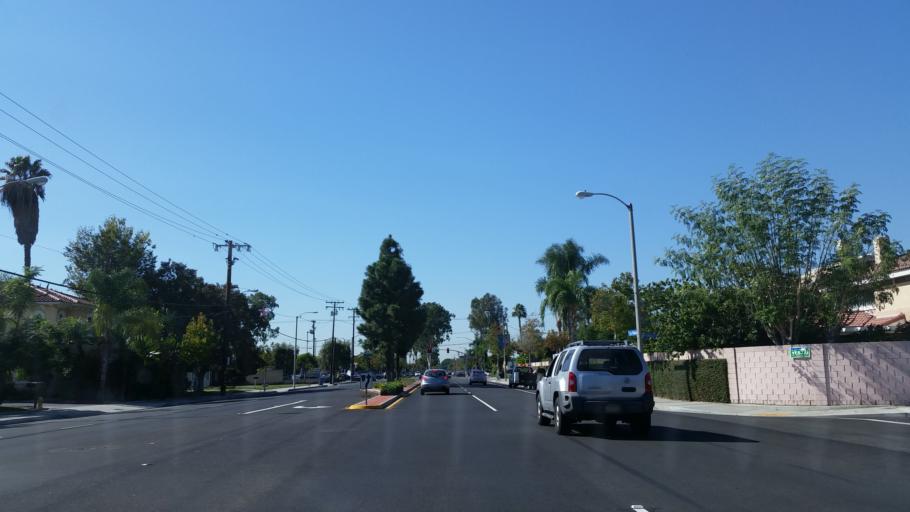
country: US
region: California
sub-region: Orange County
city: La Palma
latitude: 33.8464
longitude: -118.0439
